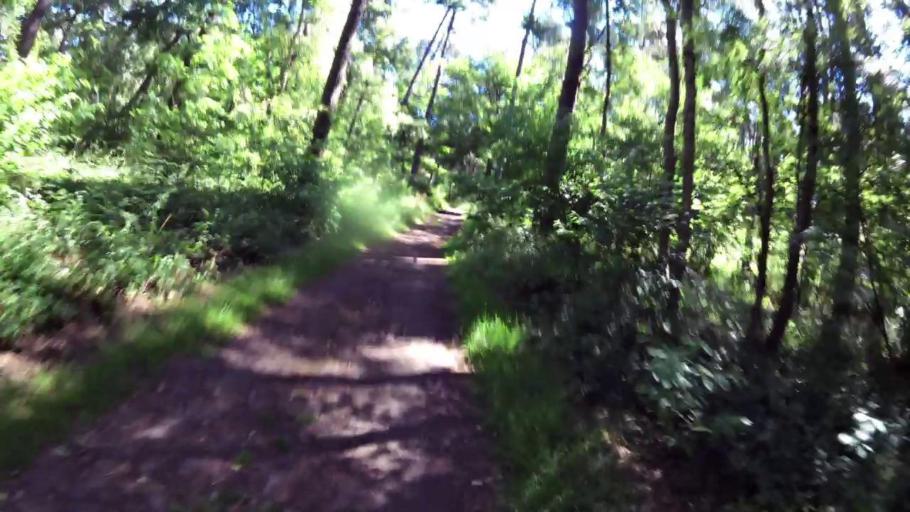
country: PL
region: West Pomeranian Voivodeship
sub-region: Powiat gryficki
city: Pobierowo
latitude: 54.0472
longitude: 14.8587
